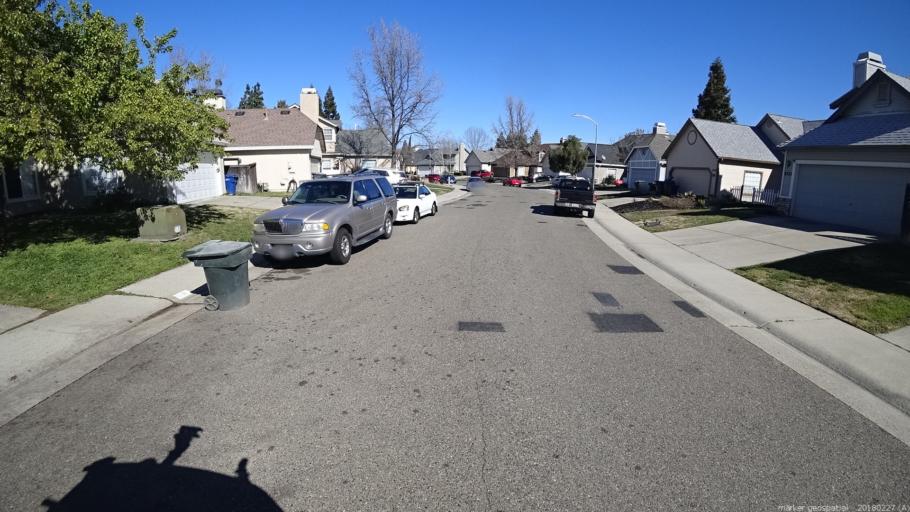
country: US
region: California
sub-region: Sacramento County
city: Antelope
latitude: 38.7173
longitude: -121.3540
